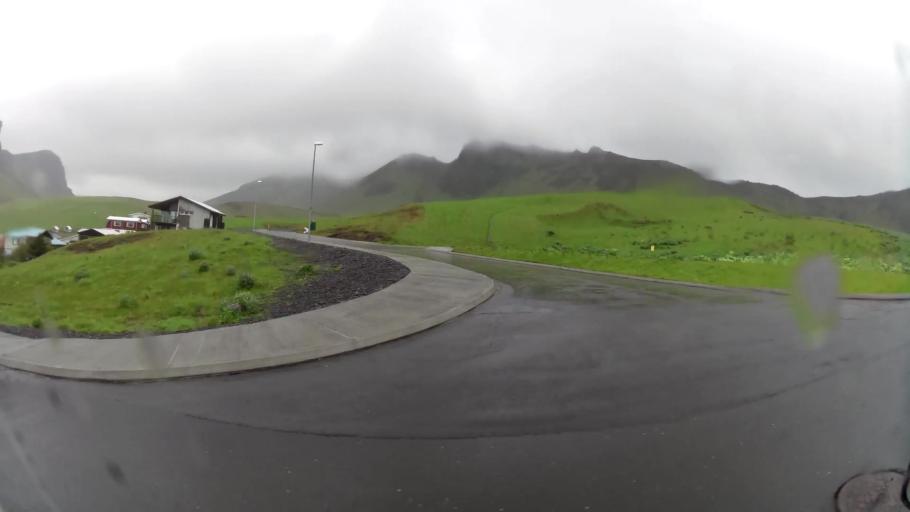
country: IS
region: South
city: Vestmannaeyjar
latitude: 63.4209
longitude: -19.0032
